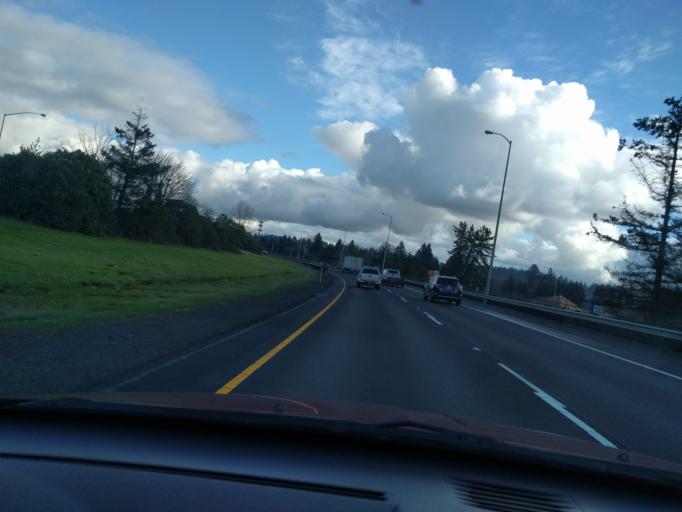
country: US
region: Oregon
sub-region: Clackamas County
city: West Linn
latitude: 45.3480
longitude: -122.6542
